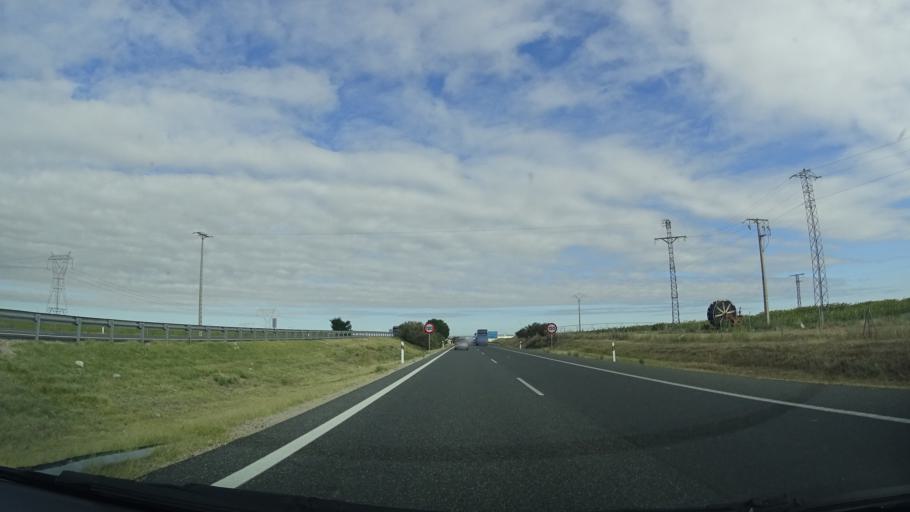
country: ES
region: Castille and Leon
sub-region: Provincia de Valladolid
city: San Vicente del Palacio
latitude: 41.2260
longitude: -4.8480
